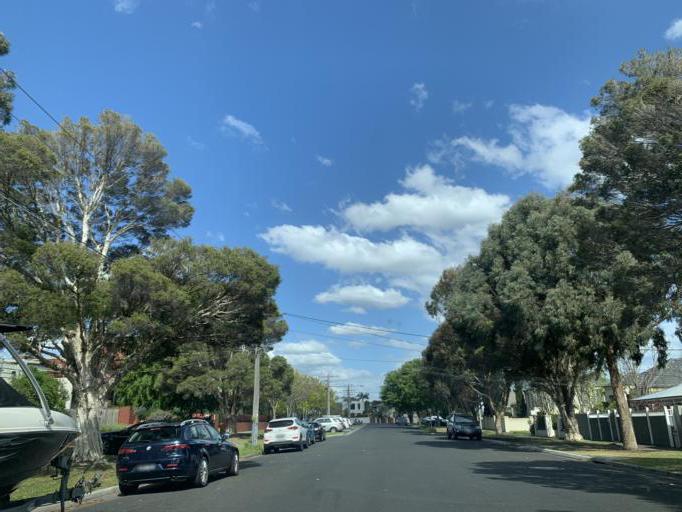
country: AU
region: Victoria
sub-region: Bayside
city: North Brighton
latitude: -37.9105
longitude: 144.9969
